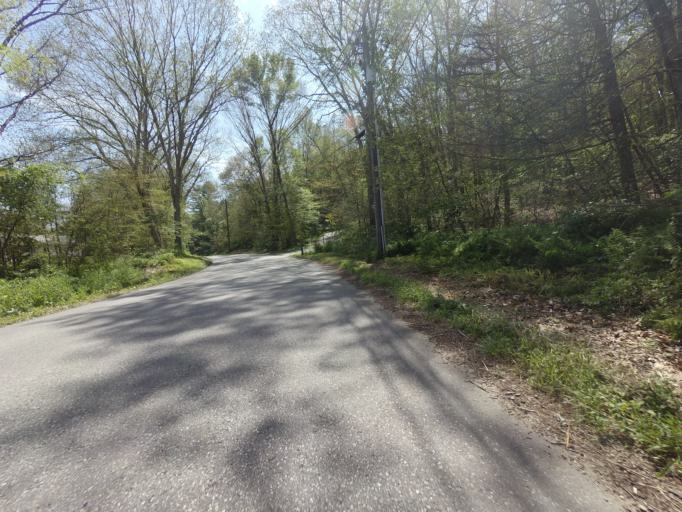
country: US
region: Connecticut
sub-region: Windham County
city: East Brooklyn
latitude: 41.8316
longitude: -71.9359
